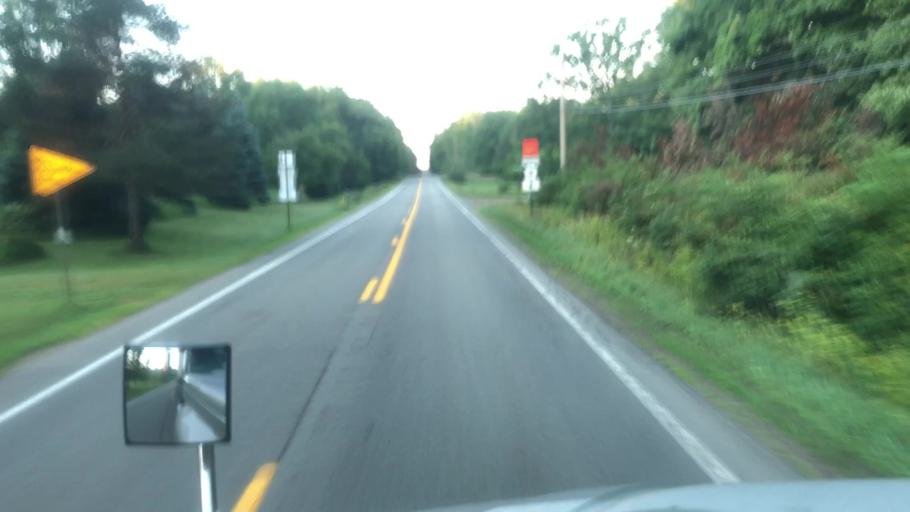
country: US
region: Pennsylvania
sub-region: Crawford County
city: Titusville
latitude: 41.5594
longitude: -79.6111
